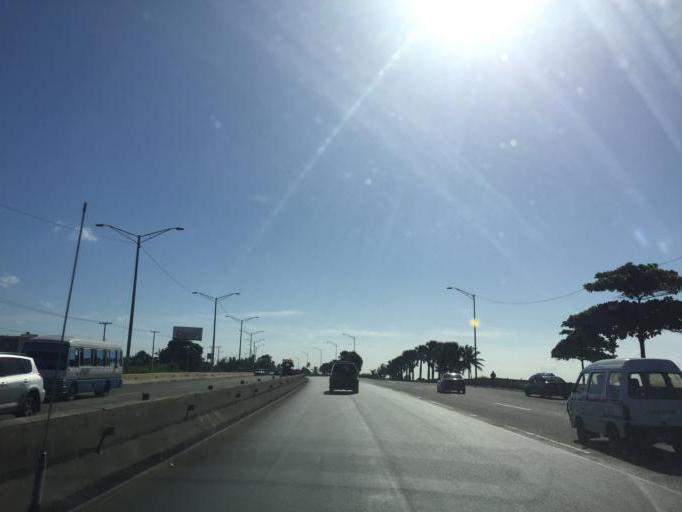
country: DO
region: Santo Domingo
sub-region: Santo Domingo
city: Santo Domingo Este
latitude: 18.4688
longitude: -69.8291
